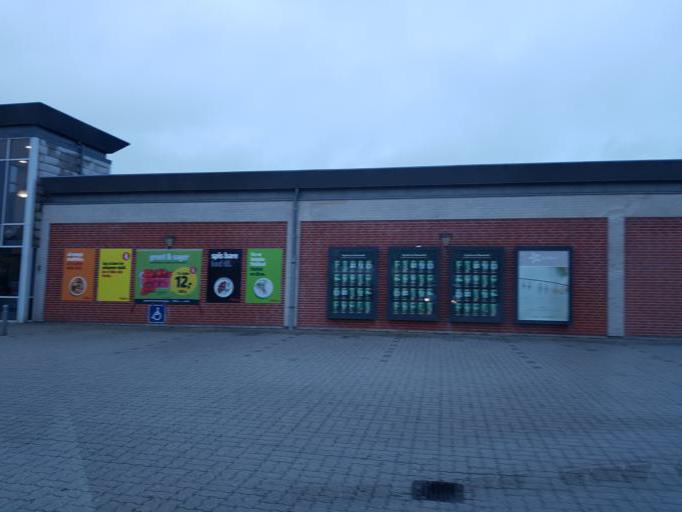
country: DK
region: South Denmark
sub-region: Esbjerg Kommune
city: Esbjerg
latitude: 55.4805
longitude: 8.4620
